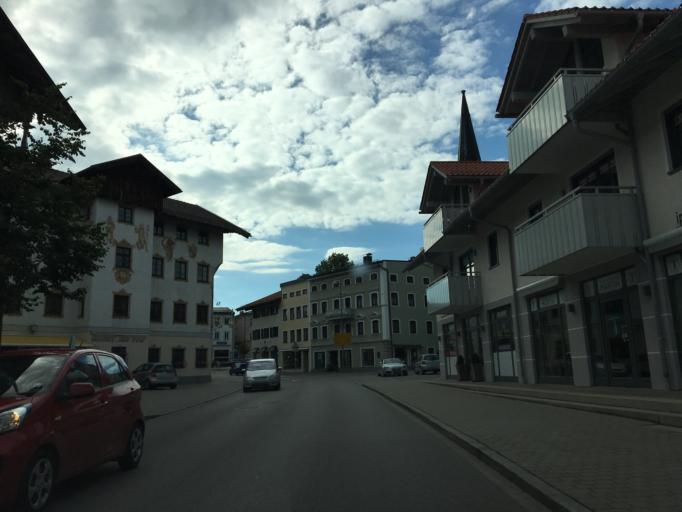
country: DE
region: Bavaria
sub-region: Upper Bavaria
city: Holzkirchen
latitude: 47.8763
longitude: 11.7024
